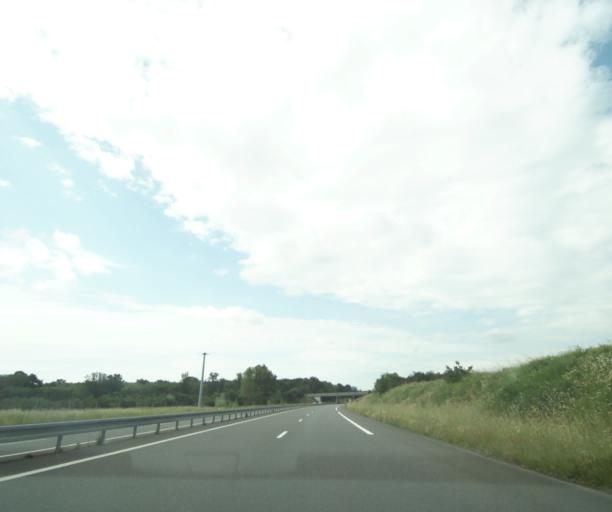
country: FR
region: Pays de la Loire
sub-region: Departement de Maine-et-Loire
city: Brion
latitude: 47.4405
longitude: -0.1745
